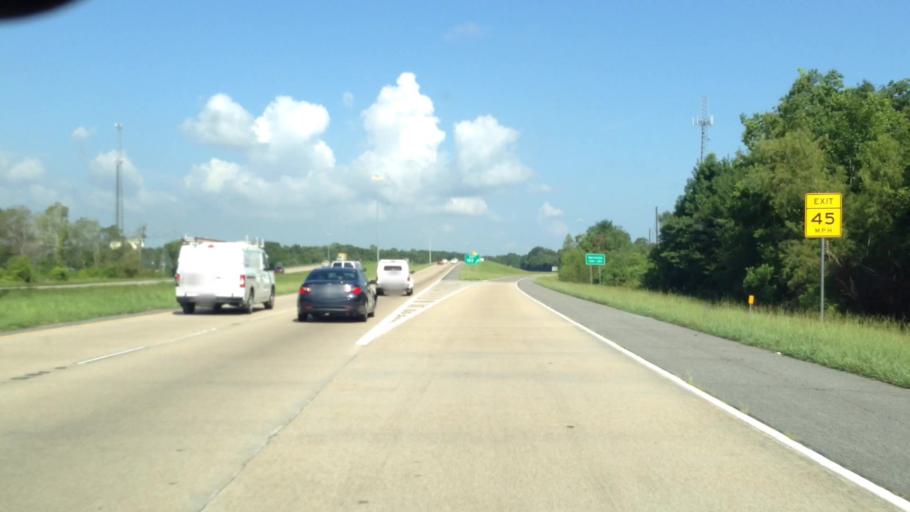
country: US
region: Louisiana
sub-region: Ascension Parish
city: Sorrento
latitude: 30.1700
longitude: -90.8708
